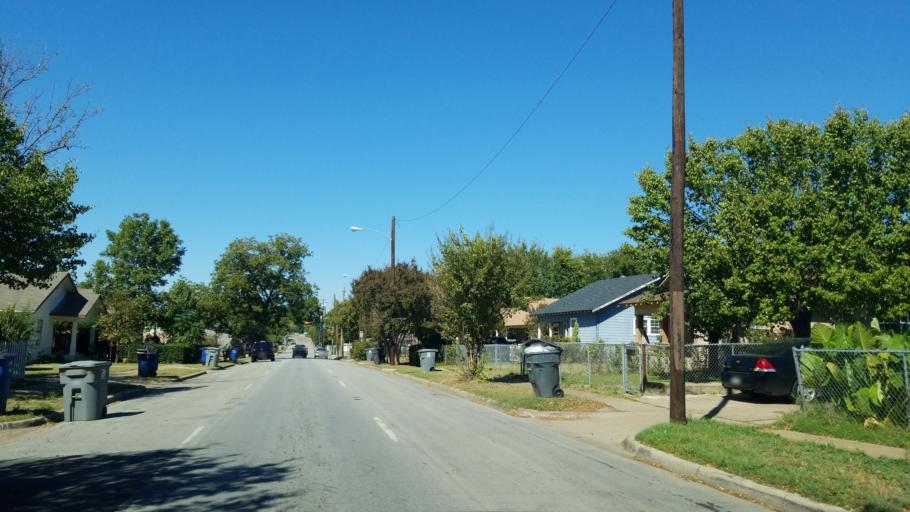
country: US
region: Texas
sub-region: Dallas County
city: Highland Park
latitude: 32.7958
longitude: -96.7497
